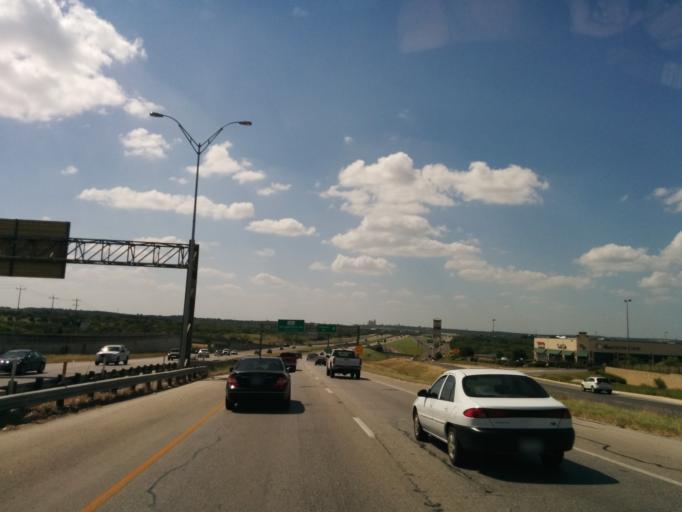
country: US
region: Texas
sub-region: Bexar County
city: Live Oak
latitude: 29.5751
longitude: -98.3392
